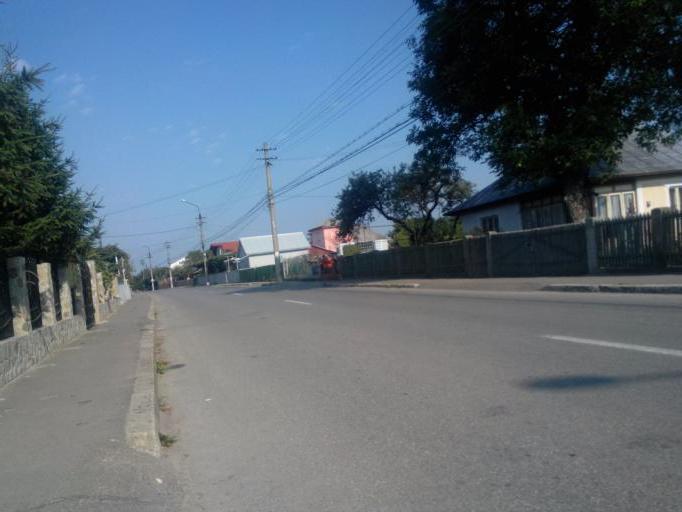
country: RO
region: Suceava
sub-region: Municipiul Falticeni
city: Falticeni
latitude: 47.4678
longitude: 26.2787
